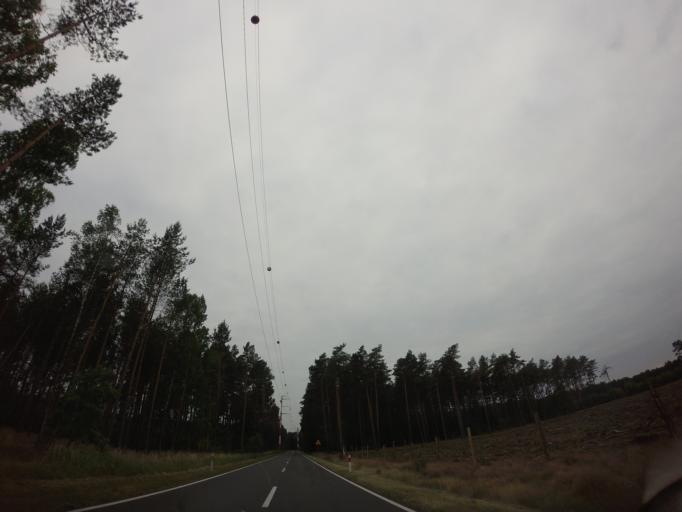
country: PL
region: West Pomeranian Voivodeship
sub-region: Powiat walecki
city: Miroslawiec
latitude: 53.3725
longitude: 16.1304
